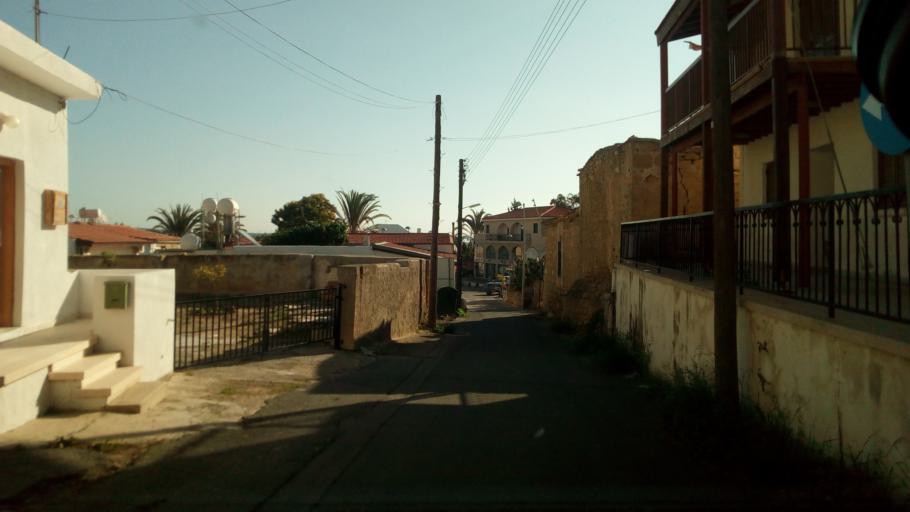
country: CY
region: Larnaka
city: Voroklini
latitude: 34.9869
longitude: 33.6499
